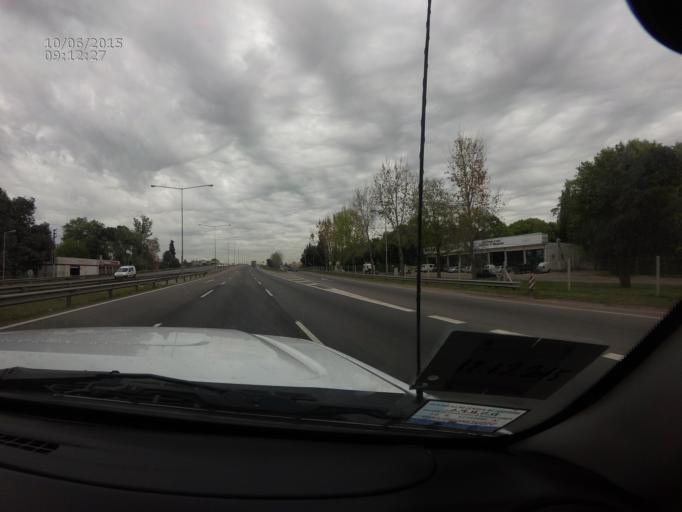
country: AR
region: Buenos Aires
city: Belen de Escobar
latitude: -34.3506
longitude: -58.8049
